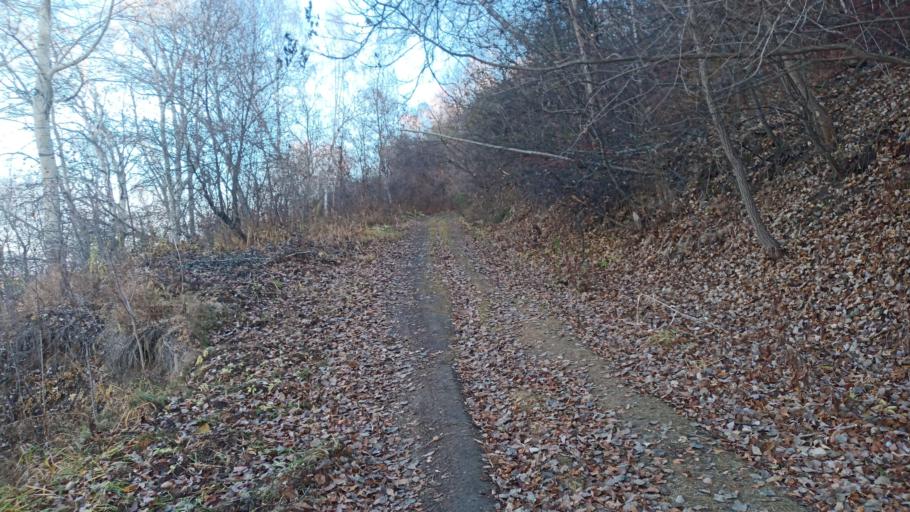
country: RU
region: Altai Krai
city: Nauchnyy Gorodok
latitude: 53.4345
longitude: 83.5474
